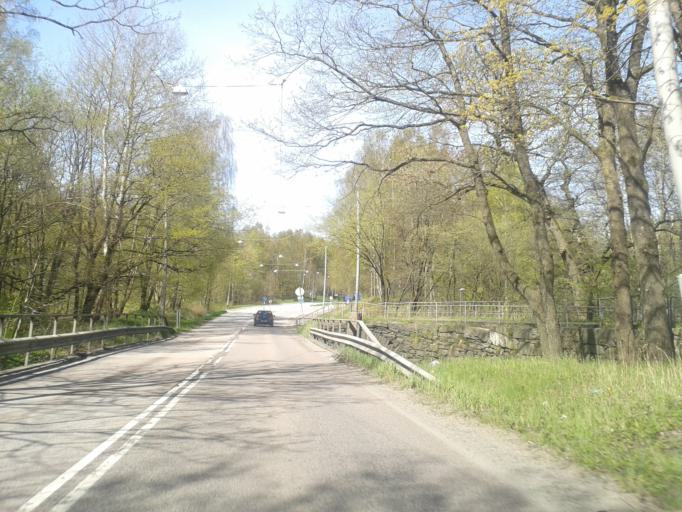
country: SE
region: Vaestra Goetaland
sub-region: Goteborg
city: Hammarkullen
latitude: 57.7614
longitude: 12.0109
